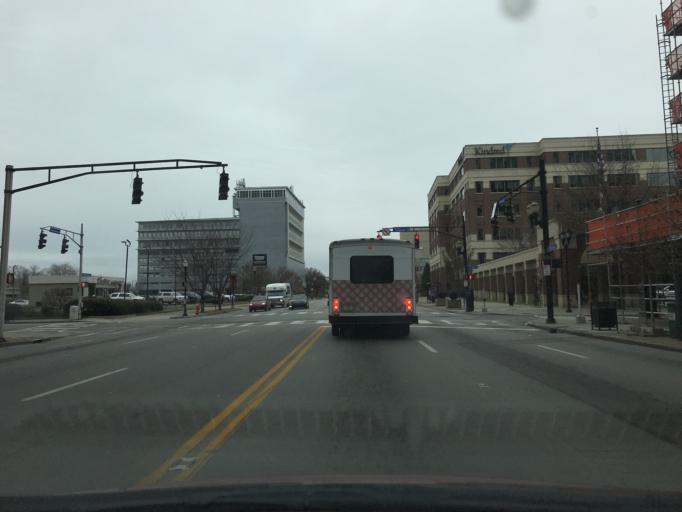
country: US
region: Kentucky
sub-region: Jefferson County
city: Louisville
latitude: 38.2461
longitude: -85.7580
